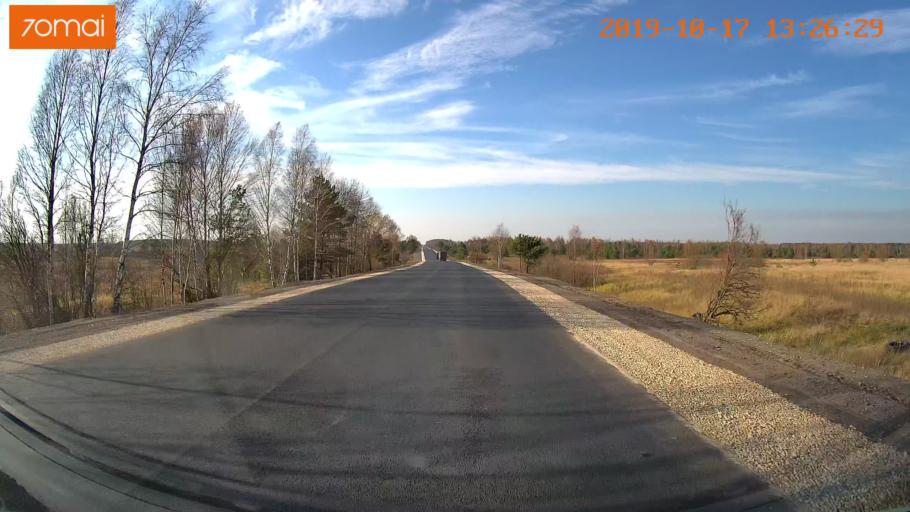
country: RU
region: Rjazan
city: Gus'-Zheleznyy
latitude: 55.1103
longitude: 40.9201
